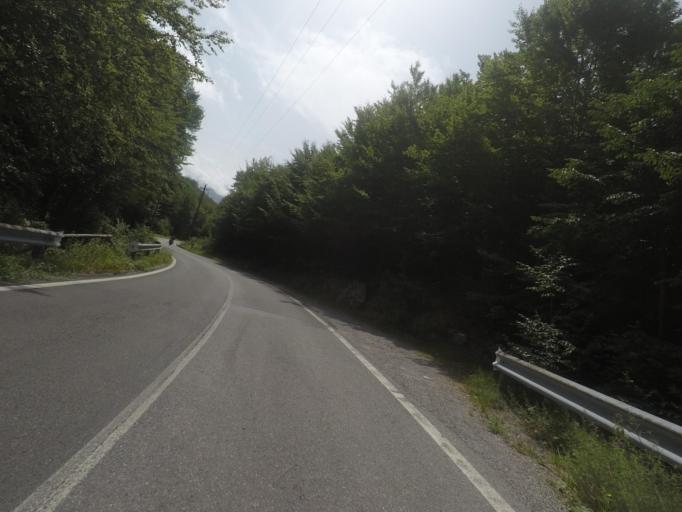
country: IT
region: Tuscany
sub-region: Provincia di Lucca
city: Seravezza
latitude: 44.0623
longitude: 10.2335
